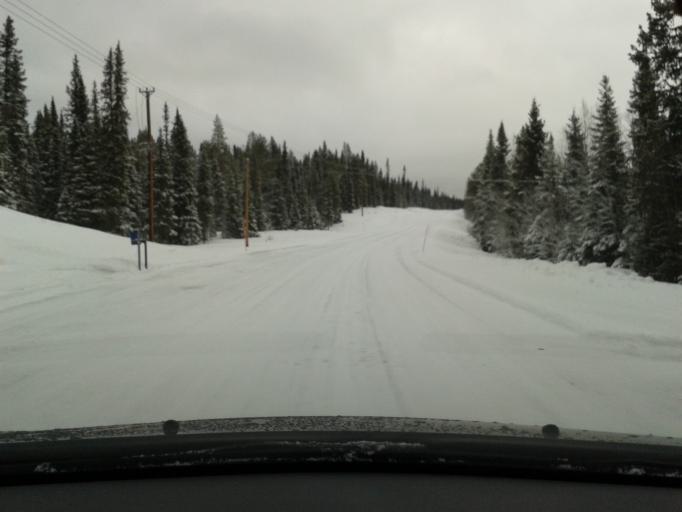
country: SE
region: Vaesterbotten
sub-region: Vilhelmina Kommun
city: Sjoberg
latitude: 65.2374
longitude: 15.8165
